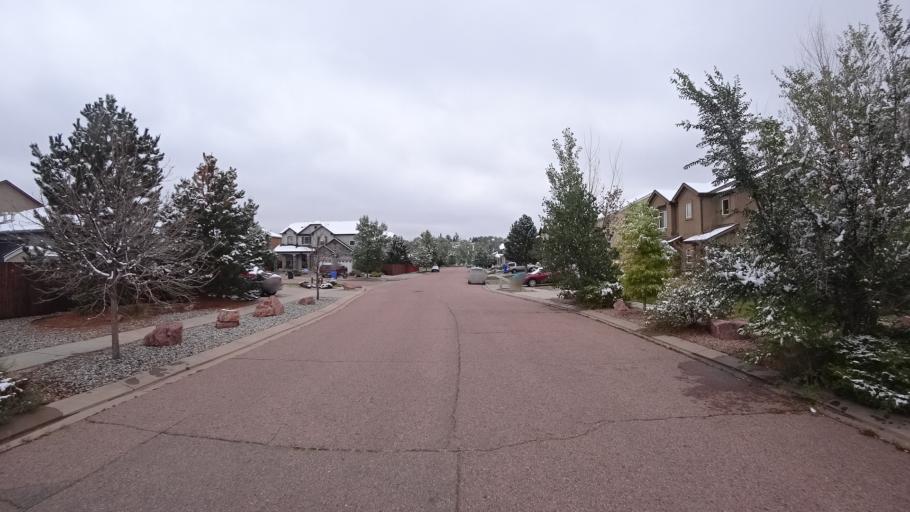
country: US
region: Colorado
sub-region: El Paso County
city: Colorado Springs
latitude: 38.9294
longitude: -104.7791
